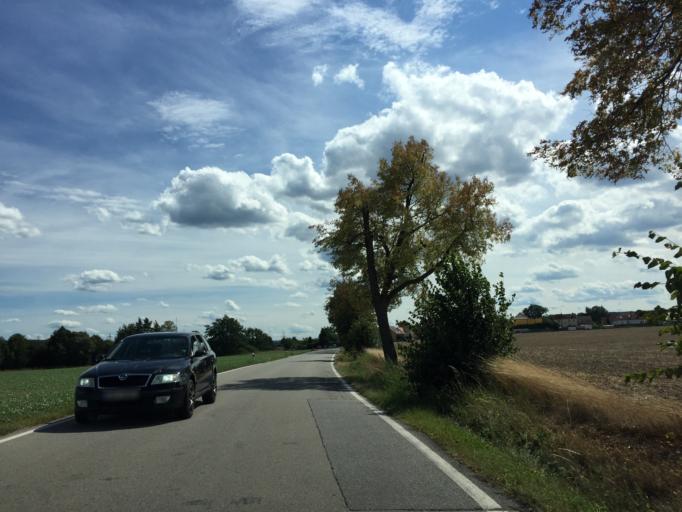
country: CZ
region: Jihocesky
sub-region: Okres Ceske Budejovice
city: Ceske Budejovice
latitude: 48.9483
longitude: 14.4825
